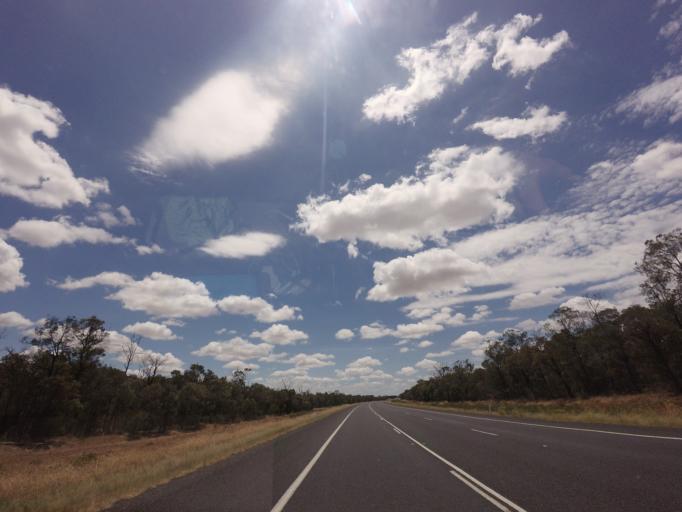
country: AU
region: New South Wales
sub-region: Moree Plains
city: Boggabilla
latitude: -28.8730
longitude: 150.1739
